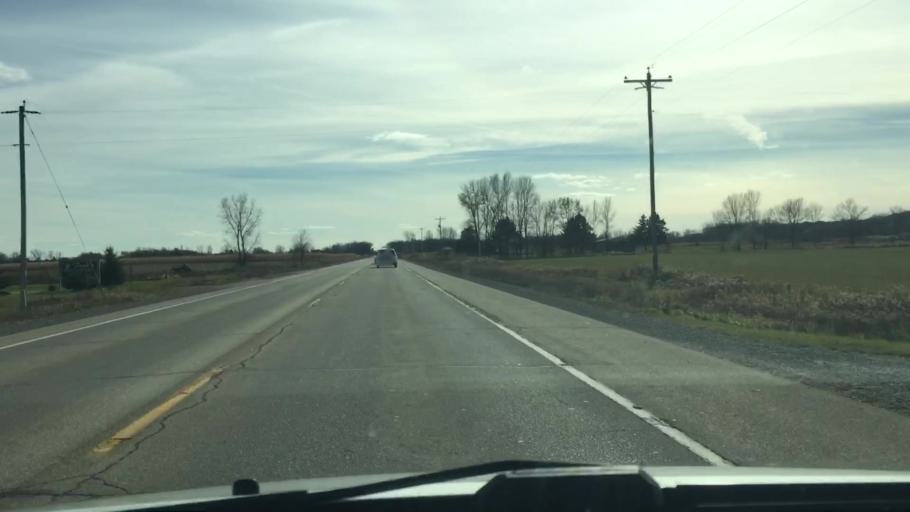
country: US
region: Wisconsin
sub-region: Brown County
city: Pulaski
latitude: 44.6272
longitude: -88.2203
